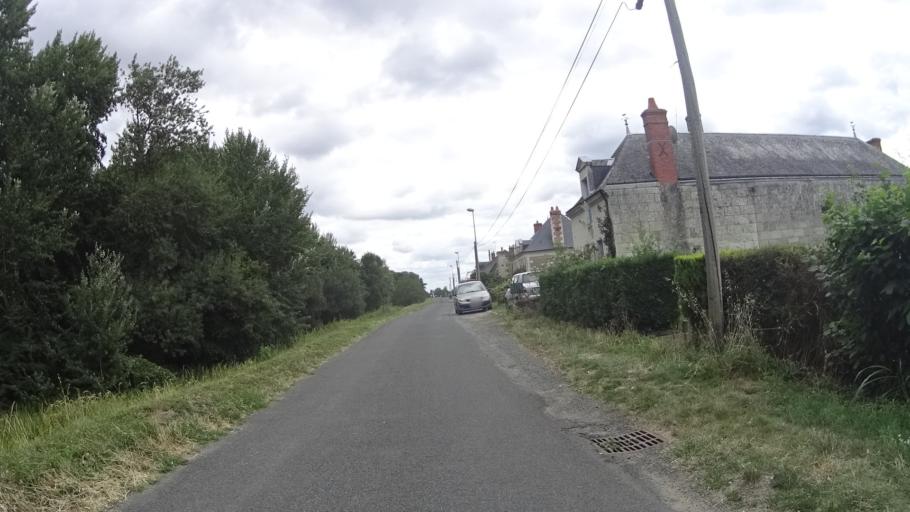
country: FR
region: Centre
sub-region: Departement d'Indre-et-Loire
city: Huismes
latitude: 47.2607
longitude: 0.2849
